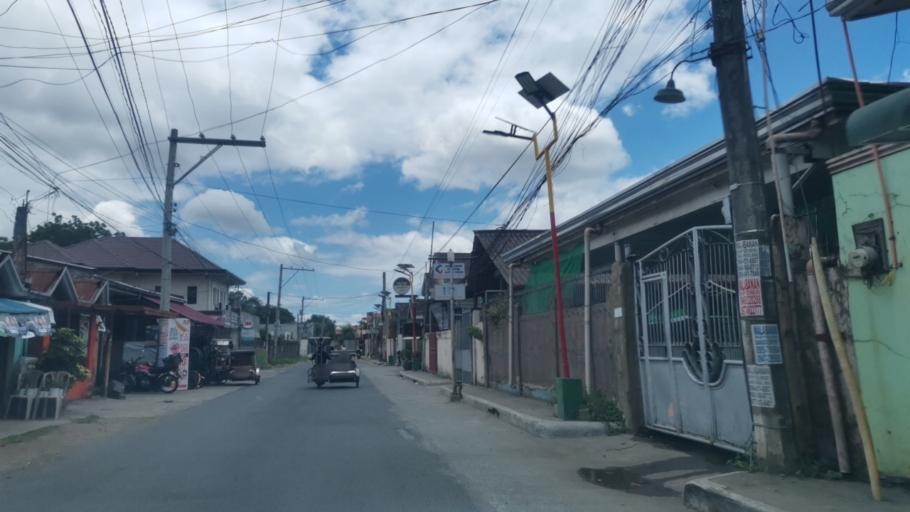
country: PH
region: Calabarzon
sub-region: Province of Batangas
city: Tanauan
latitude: 14.0801
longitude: 121.1449
